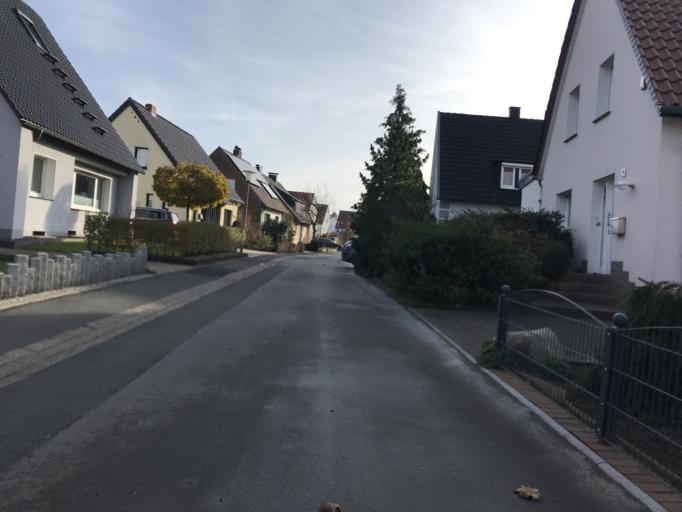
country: DE
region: North Rhine-Westphalia
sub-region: Regierungsbezirk Arnsberg
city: Hamm
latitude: 51.6893
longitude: 7.8644
